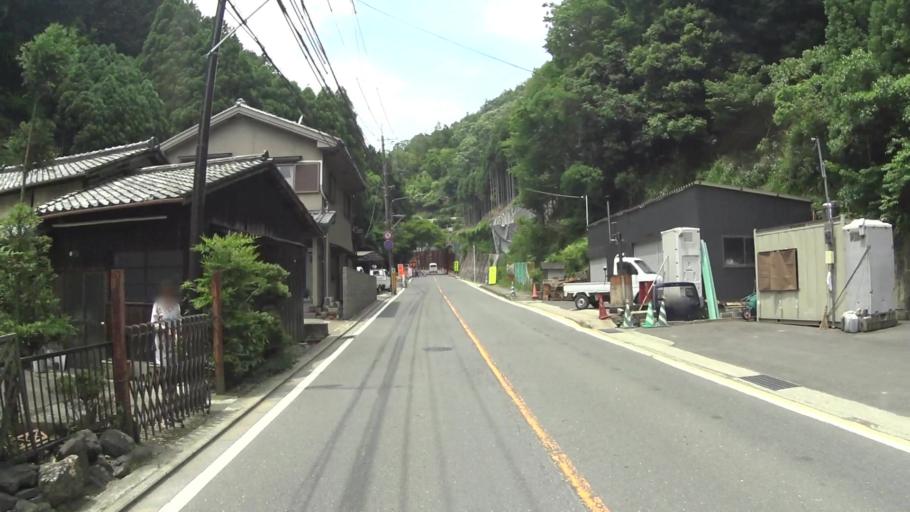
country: JP
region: Kyoto
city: Kyoto
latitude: 35.0435
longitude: 135.6855
